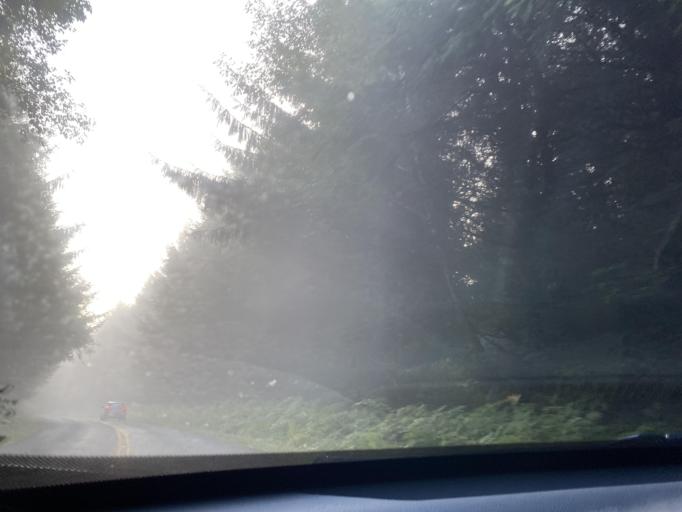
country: US
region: Washington
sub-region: Clallam County
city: Forks
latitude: 47.8082
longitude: -124.0941
